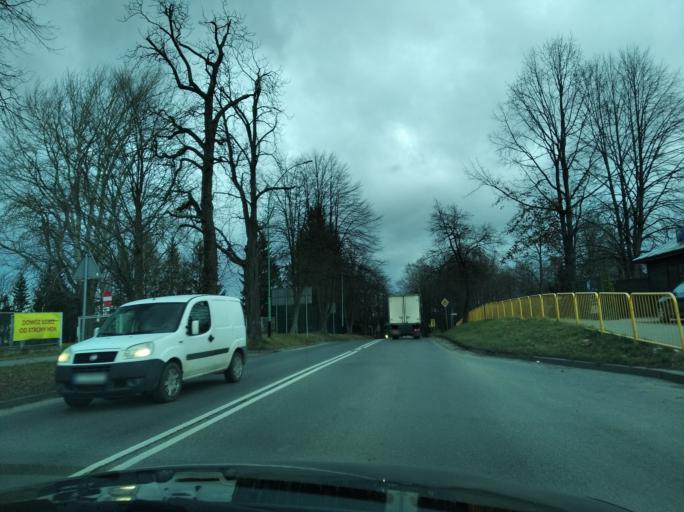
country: PL
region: Subcarpathian Voivodeship
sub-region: Powiat lancucki
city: Lancut
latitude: 50.0714
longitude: 22.2373
